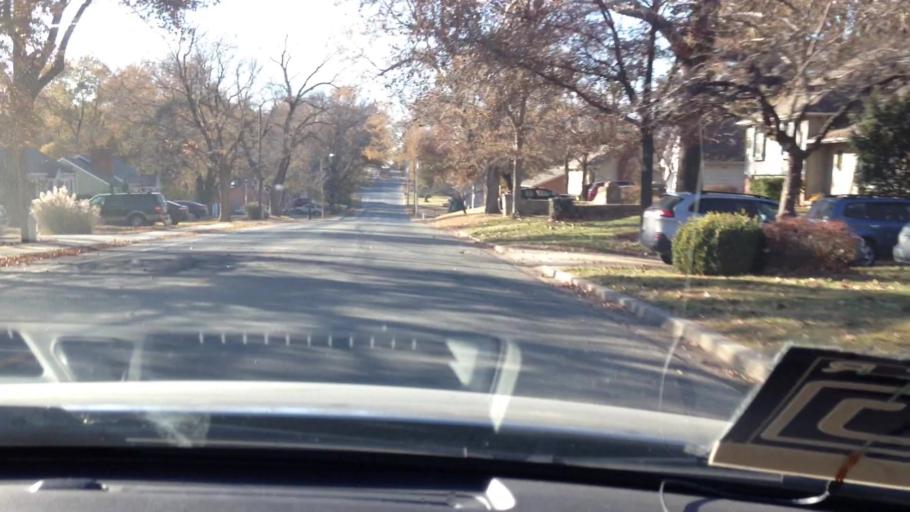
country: US
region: Kansas
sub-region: Johnson County
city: Overland Park
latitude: 38.9858
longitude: -94.6805
